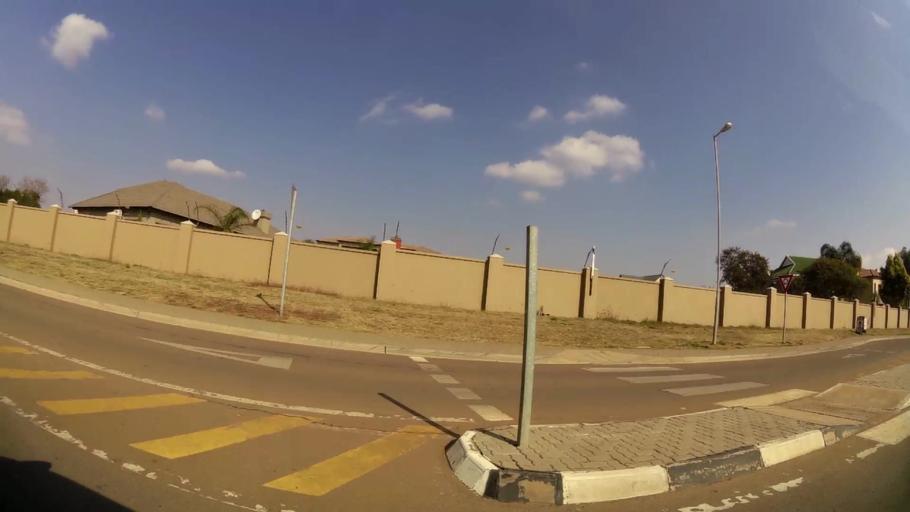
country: ZA
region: Gauteng
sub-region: City of Tshwane Metropolitan Municipality
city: Cullinan
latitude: -25.7760
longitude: 28.3782
